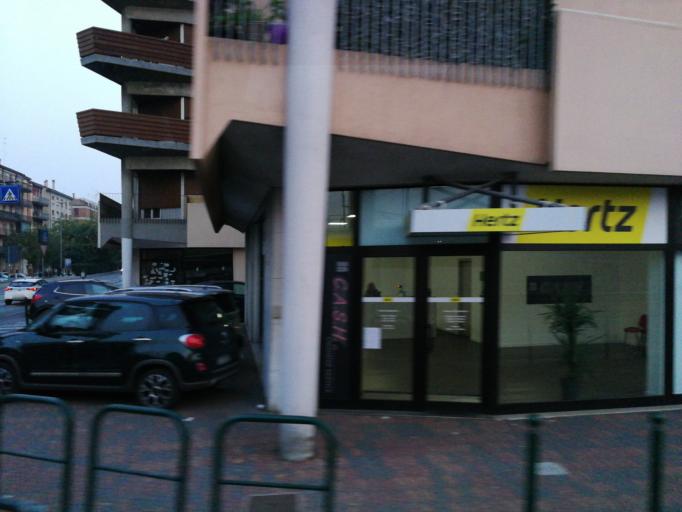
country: IT
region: Veneto
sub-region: Provincia di Venezia
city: Mestre
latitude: 45.4826
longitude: 12.2357
